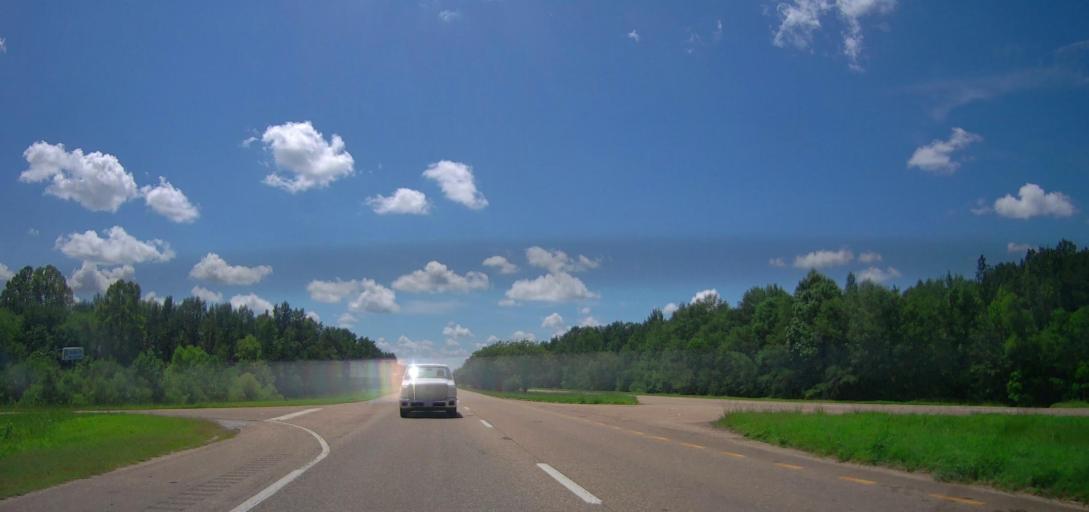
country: US
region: Alabama
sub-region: Montgomery County
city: Montgomery
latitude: 32.4220
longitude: -86.2475
